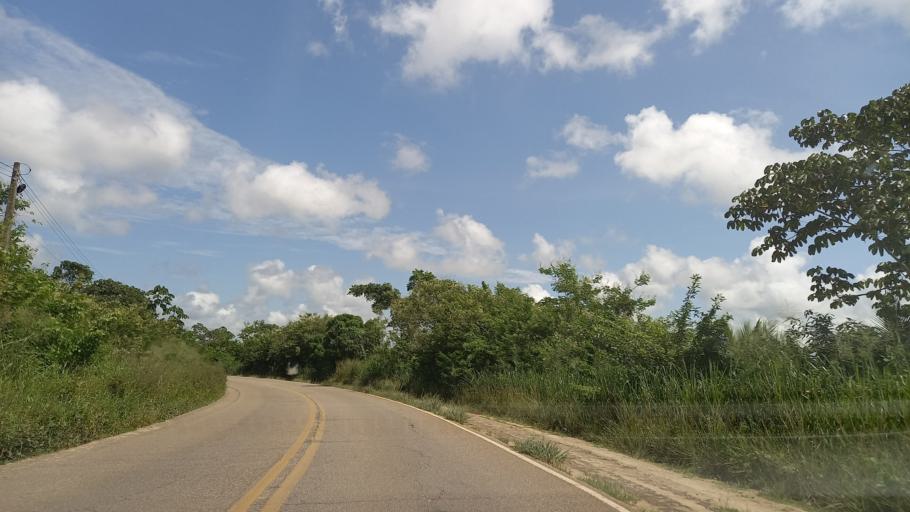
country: BR
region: Pernambuco
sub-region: Barreiros
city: Barreiros
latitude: -8.7959
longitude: -35.1901
